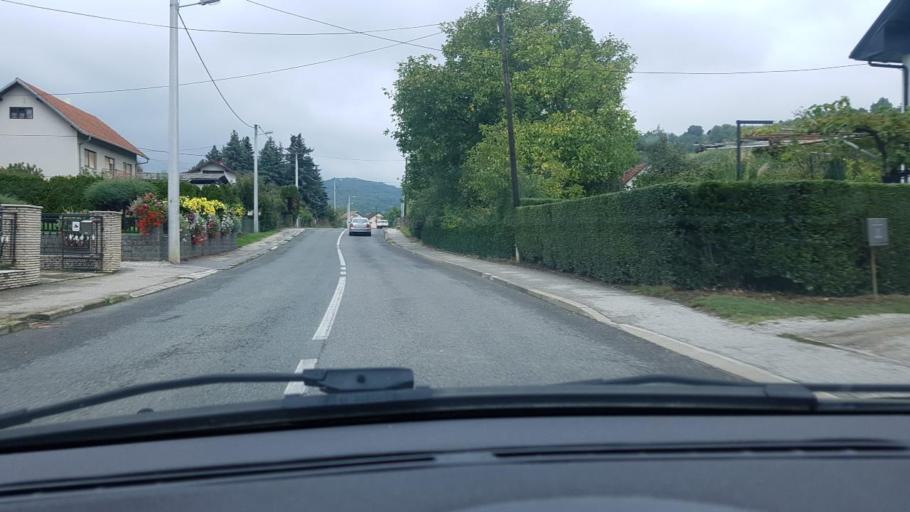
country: HR
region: Grad Zagreb
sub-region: Sesvete
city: Sesvete
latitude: 45.9124
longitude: 16.1246
